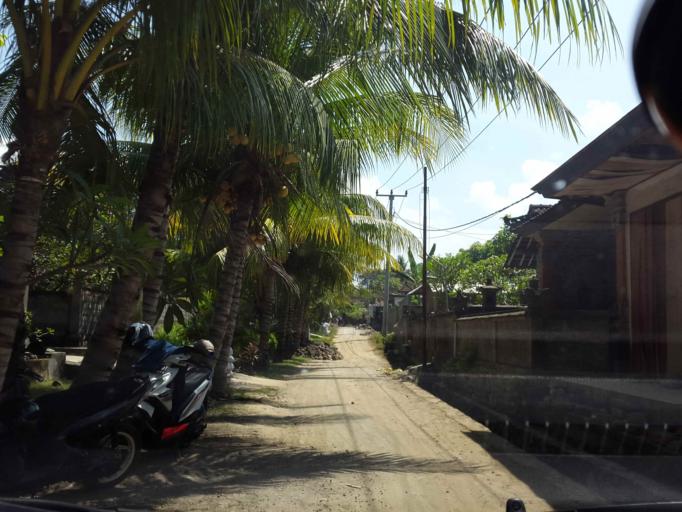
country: ID
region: Bali
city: Klungkung
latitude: -8.5719
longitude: 115.3751
